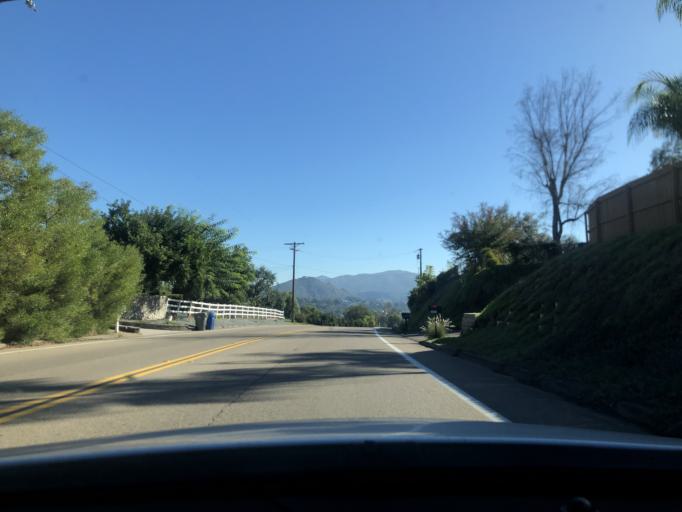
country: US
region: California
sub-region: San Diego County
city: Rancho San Diego
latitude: 32.7715
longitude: -116.9374
